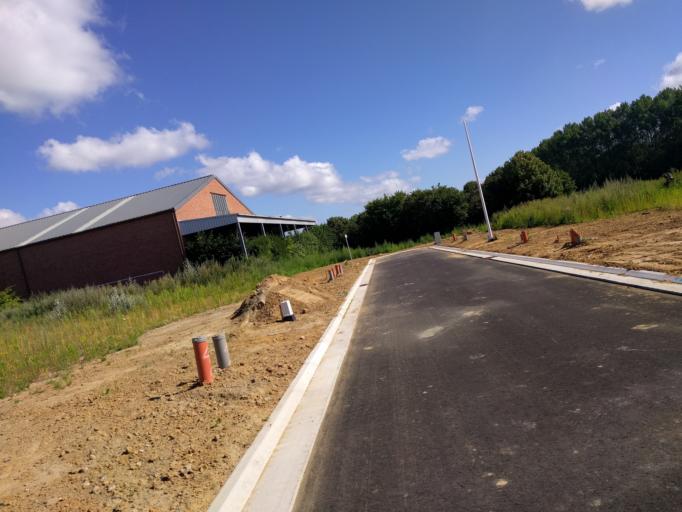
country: BE
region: Flanders
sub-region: Provincie West-Vlaanderen
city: Wevelgem
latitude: 50.8367
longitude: 3.1937
